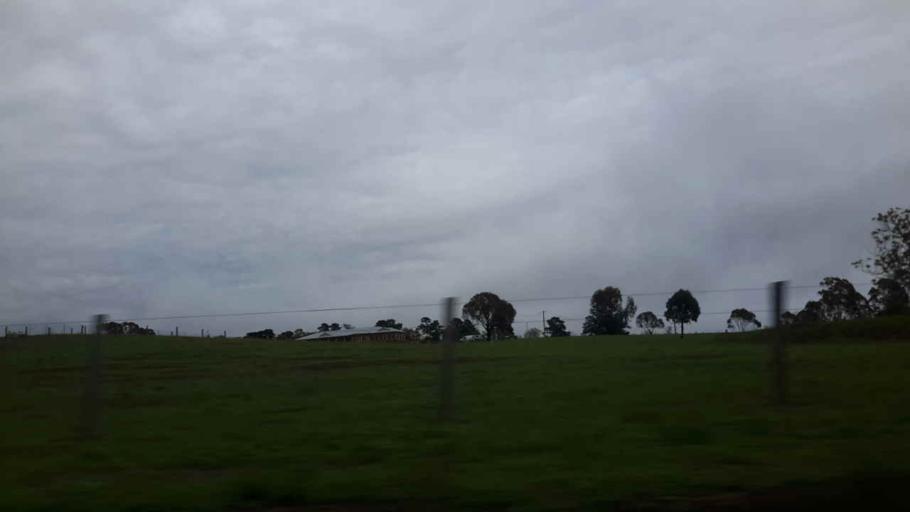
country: AU
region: New South Wales
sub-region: Wollondilly
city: Douglas Park
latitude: -34.1431
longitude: 150.7170
